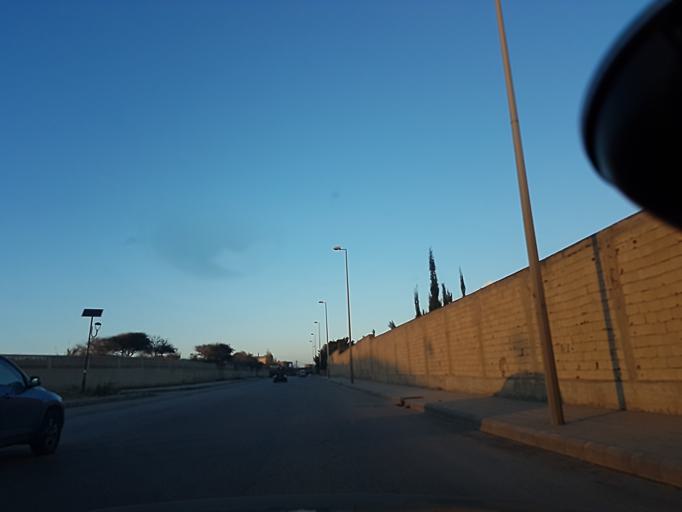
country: LB
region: Liban-Sud
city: Sidon
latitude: 33.5511
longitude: 35.3661
